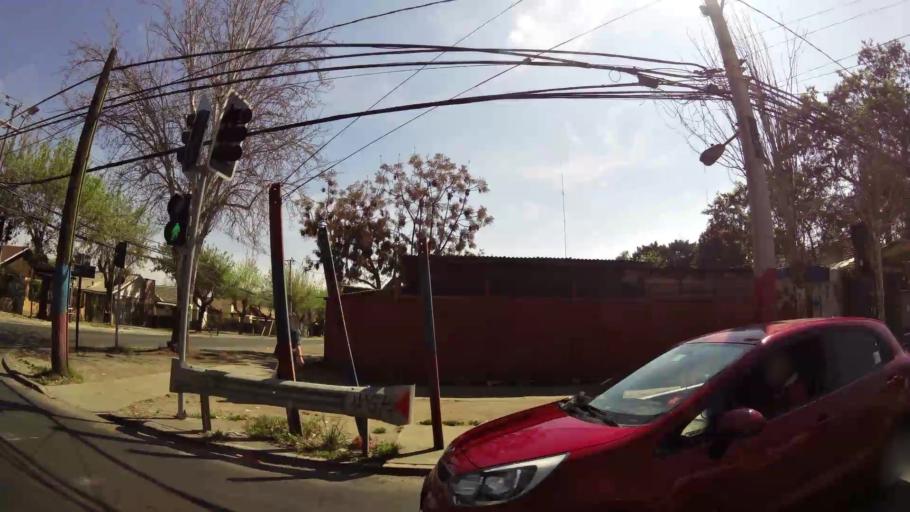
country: CL
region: Santiago Metropolitan
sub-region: Provincia de Santiago
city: Villa Presidente Frei, Nunoa, Santiago, Chile
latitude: -33.4862
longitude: -70.5897
